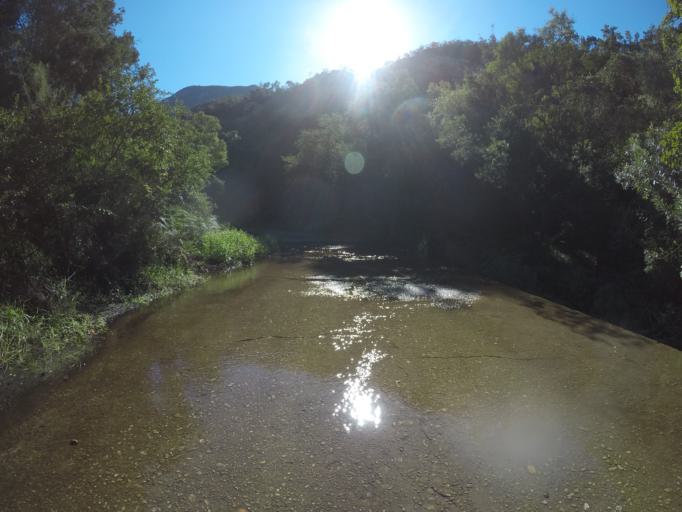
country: ZA
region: Eastern Cape
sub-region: Cacadu District Municipality
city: Kareedouw
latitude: -33.6570
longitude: 24.5265
